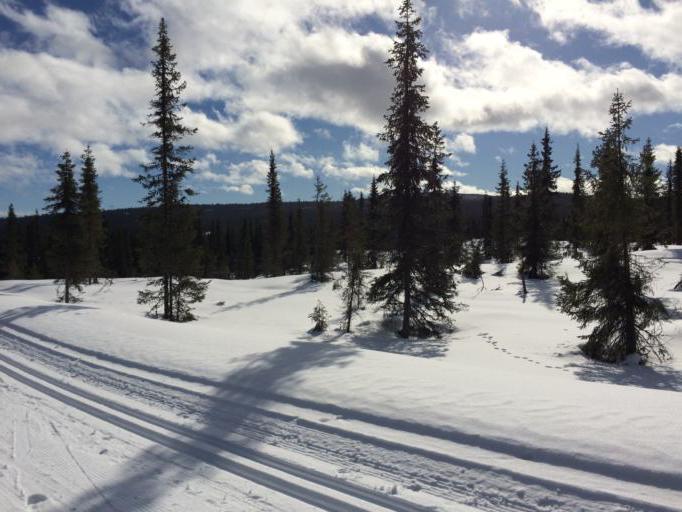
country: NO
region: Oppland
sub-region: Gausdal
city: Segalstad bru
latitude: 61.3306
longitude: 10.0921
